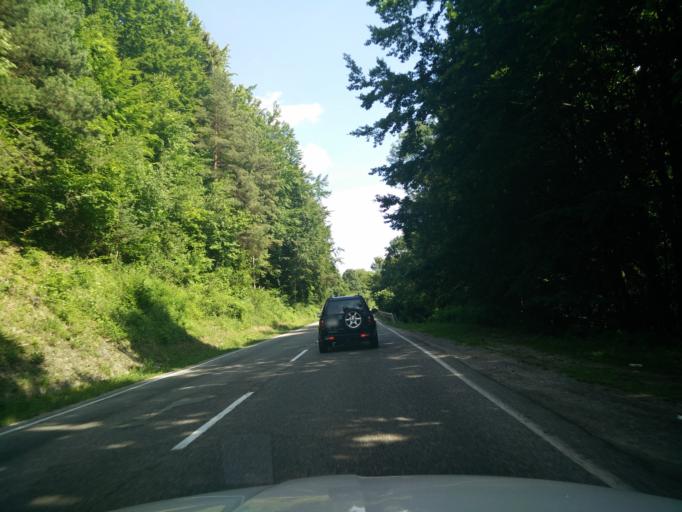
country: SK
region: Nitriansky
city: Prievidza
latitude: 48.8882
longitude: 18.7018
